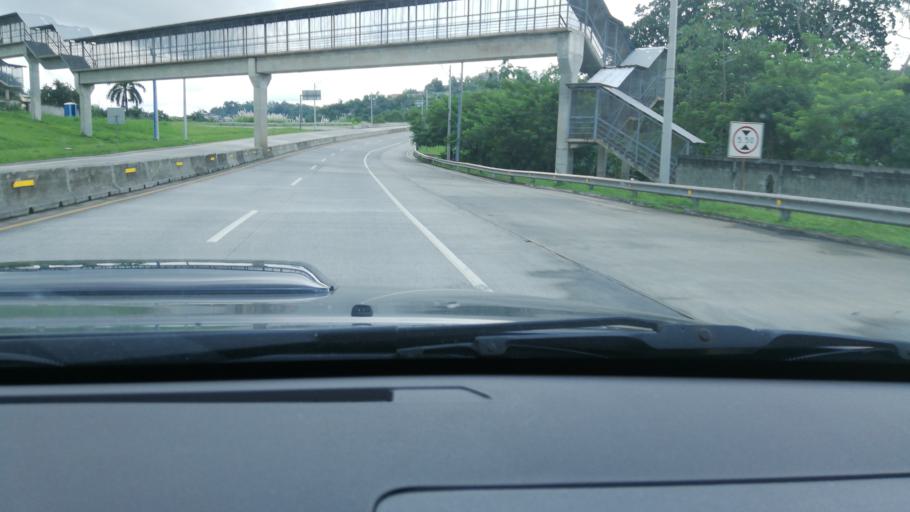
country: PA
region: Panama
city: San Miguelito
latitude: 9.0654
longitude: -79.4734
